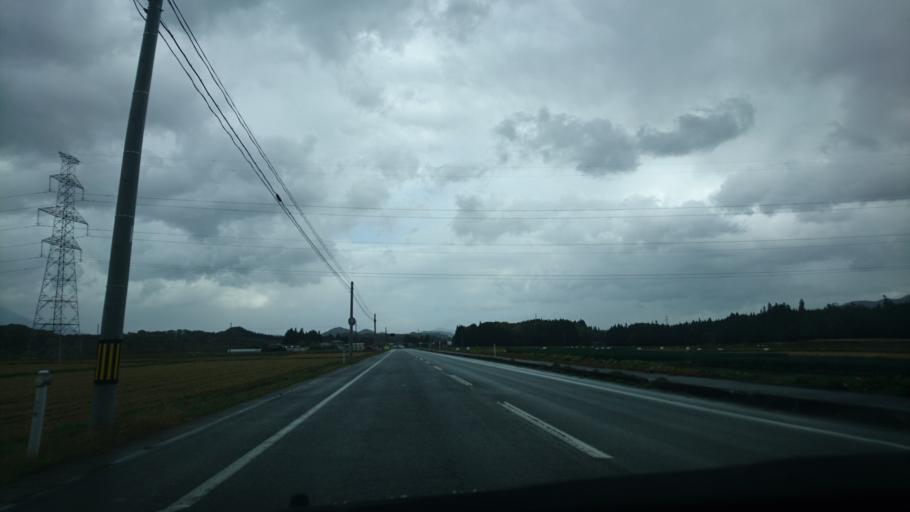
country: JP
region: Iwate
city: Shizukuishi
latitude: 39.6554
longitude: 140.9580
